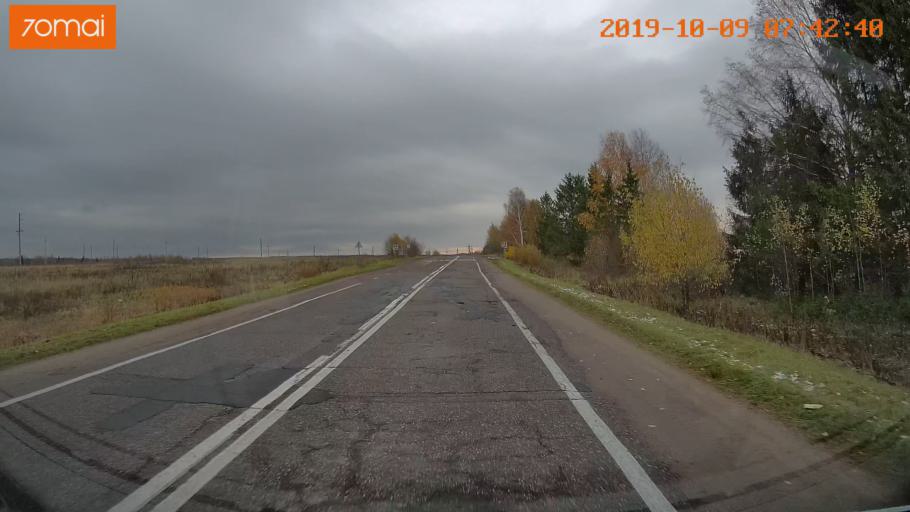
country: RU
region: Jaroslavl
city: Kukoboy
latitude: 58.6437
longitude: 39.7248
